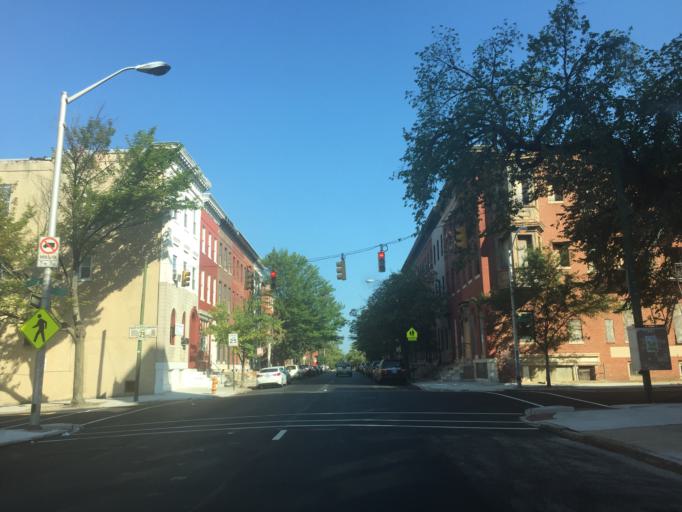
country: US
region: Maryland
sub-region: City of Baltimore
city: Baltimore
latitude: 39.3032
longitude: -76.6285
